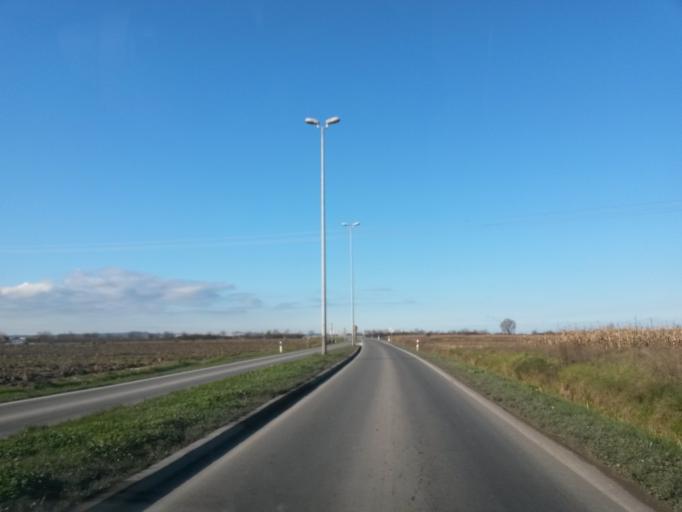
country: HR
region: Virovitick-Podravska
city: Slatina
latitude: 45.7148
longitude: 17.7121
